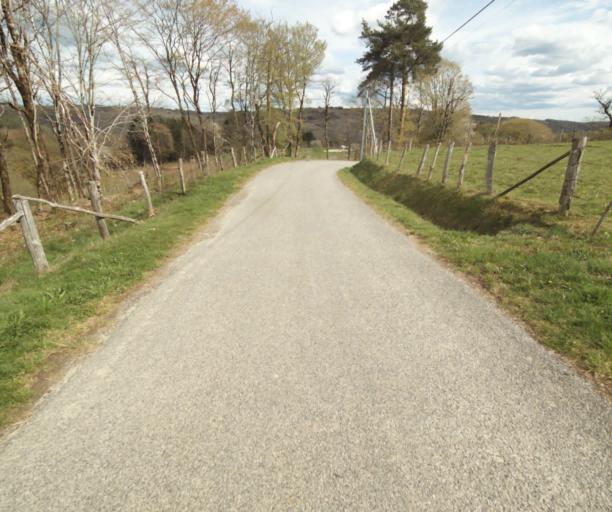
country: FR
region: Limousin
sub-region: Departement de la Correze
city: Argentat
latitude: 45.1802
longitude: 1.9447
